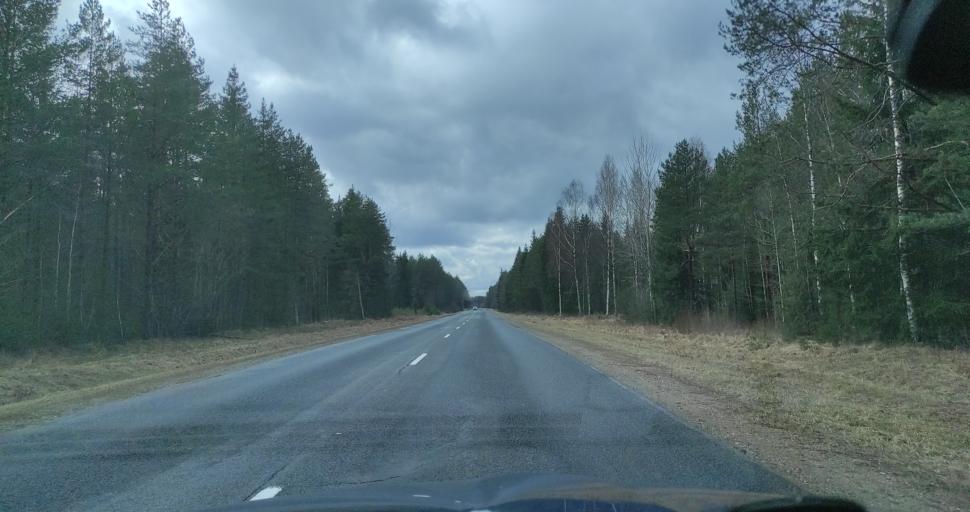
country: LV
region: Talsu Rajons
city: Stende
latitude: 57.1117
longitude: 22.5027
